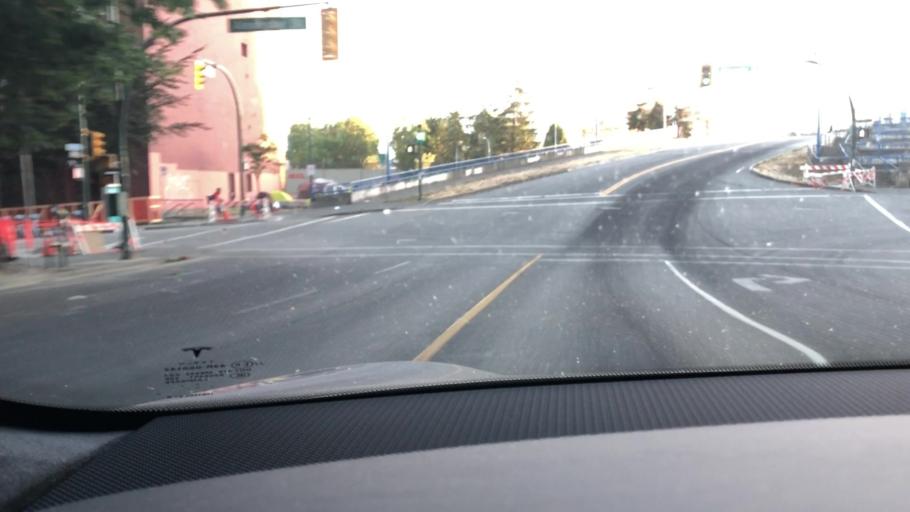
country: CA
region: British Columbia
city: West End
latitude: 49.2838
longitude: -123.0995
